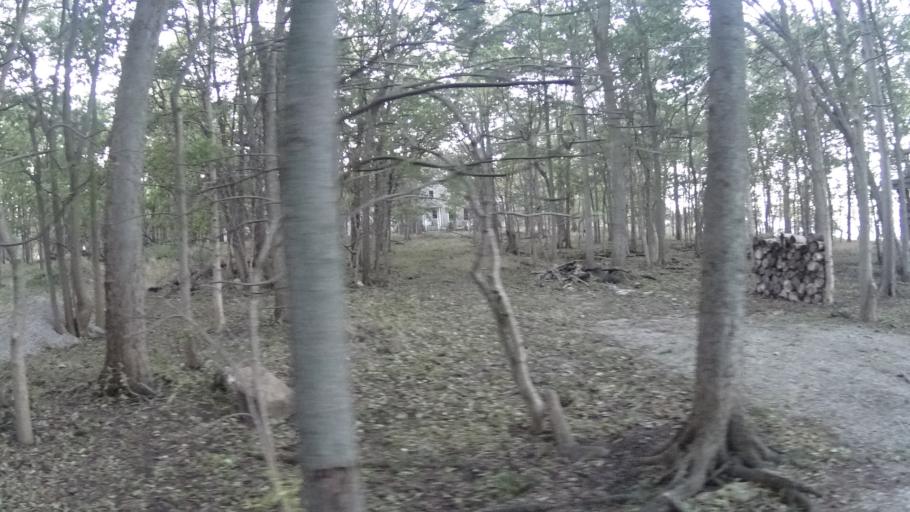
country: US
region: Ohio
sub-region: Erie County
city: Sandusky
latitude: 41.6221
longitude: -82.6764
